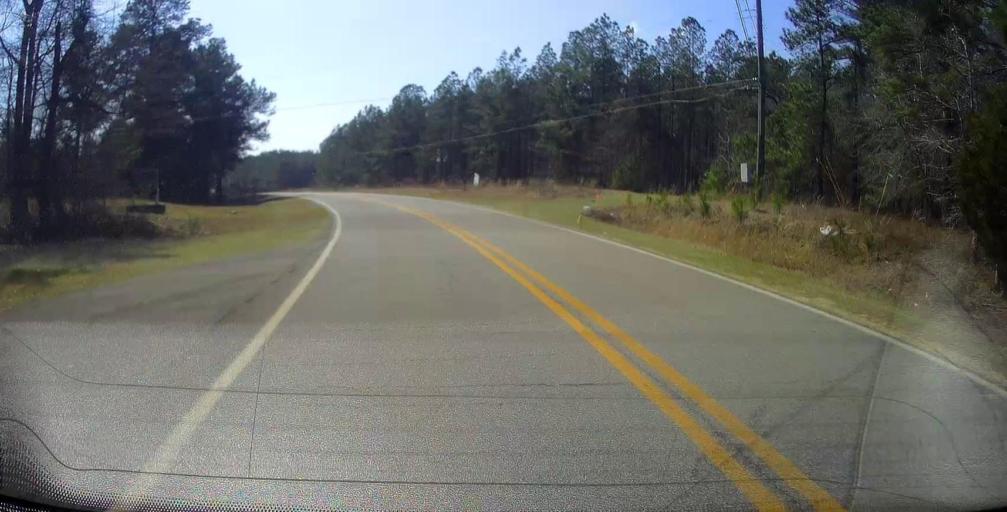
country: US
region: Georgia
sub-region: Jones County
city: Gray
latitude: 32.9139
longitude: -83.5383
